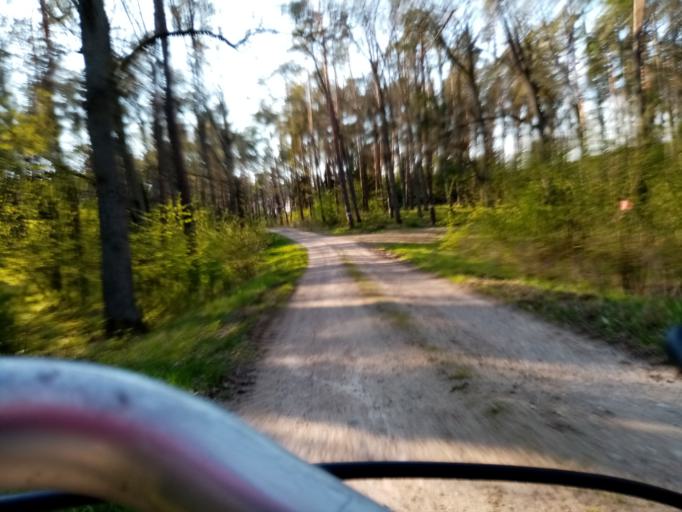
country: PL
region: Kujawsko-Pomorskie
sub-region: Powiat brodnicki
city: Gorzno
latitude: 53.1619
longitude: 19.6803
